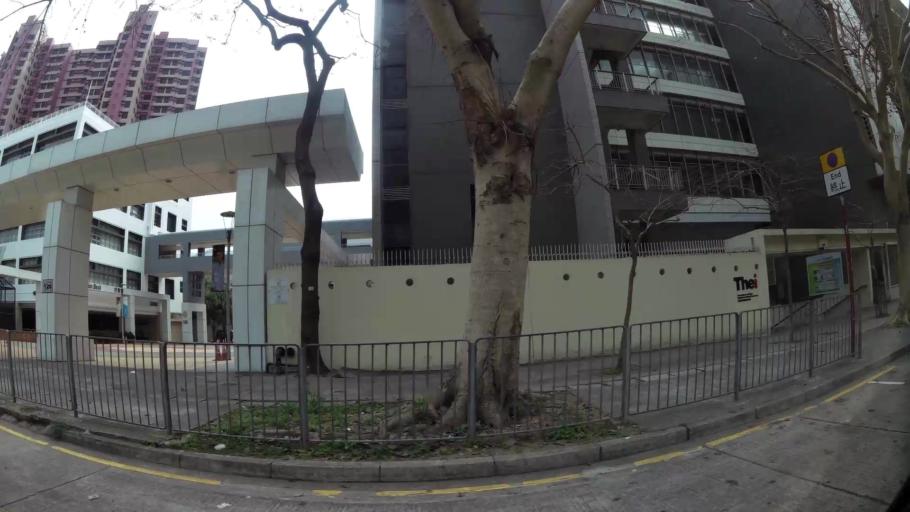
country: HK
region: Wanchai
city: Wan Chai
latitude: 22.2724
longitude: 114.2394
